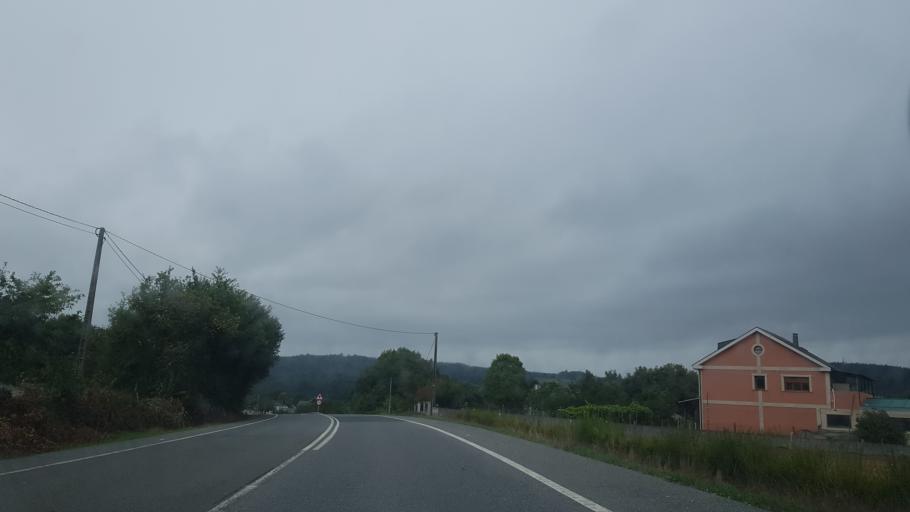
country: ES
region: Galicia
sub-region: Provincia de Lugo
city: Lugo
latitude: 42.9941
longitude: -7.6025
